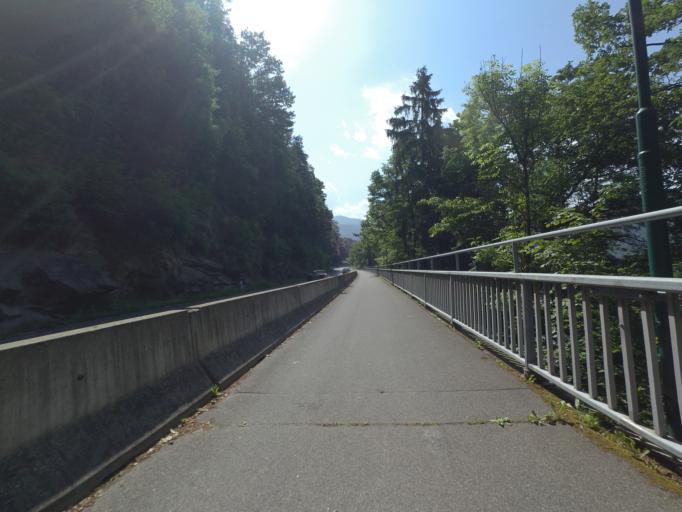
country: AT
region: Carinthia
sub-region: Politischer Bezirk Villach Land
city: Ferndorf
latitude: 46.7798
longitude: 13.6263
